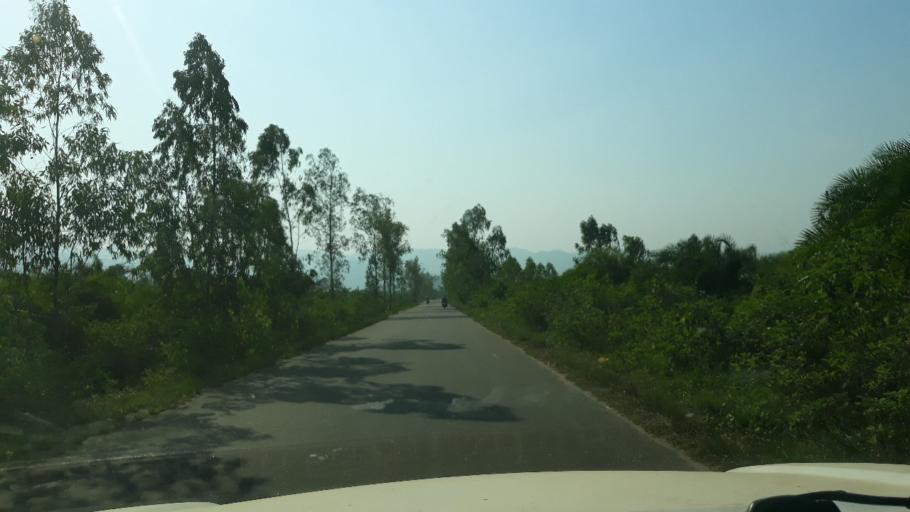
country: BI
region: Cibitoke
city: Cibitoke
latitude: -2.8139
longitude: 29.0039
